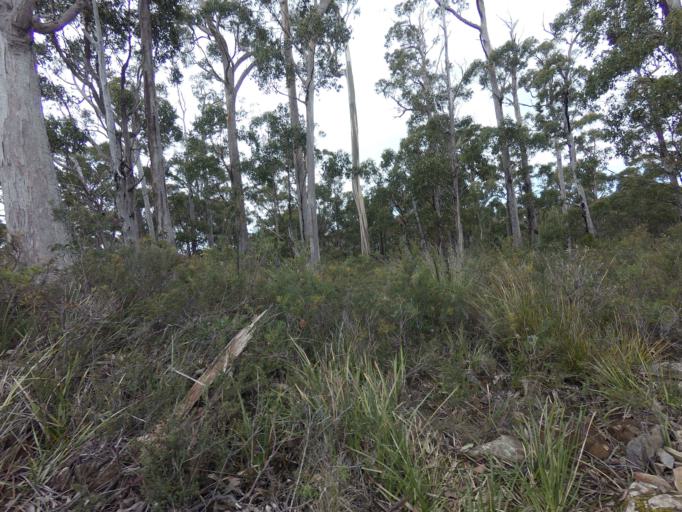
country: AU
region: Tasmania
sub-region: Huon Valley
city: Geeveston
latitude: -43.4716
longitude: 146.9318
